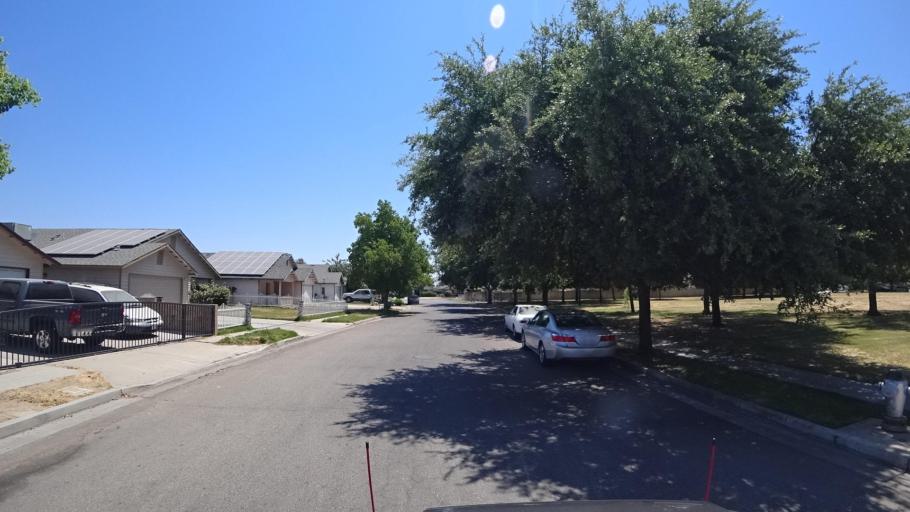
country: US
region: California
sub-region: Fresno County
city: West Park
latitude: 36.7087
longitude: -119.8173
